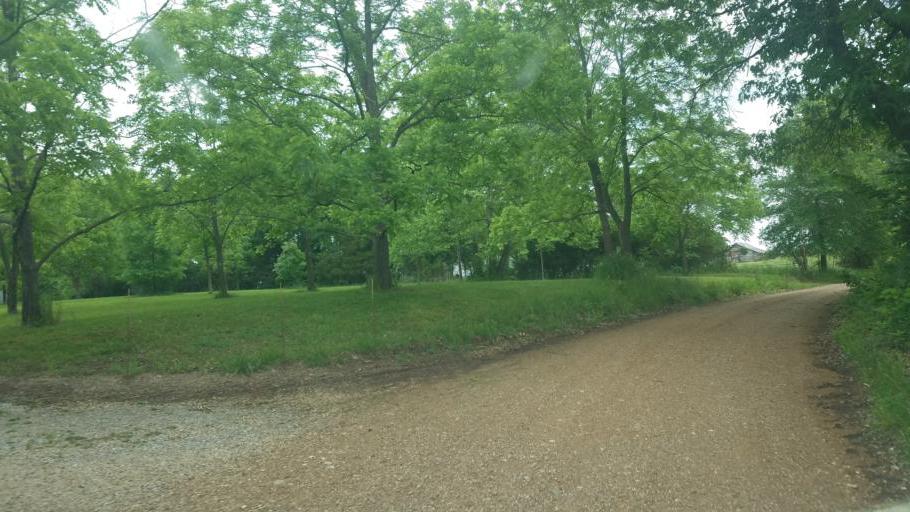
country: US
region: Missouri
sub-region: Moniteau County
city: California
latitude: 38.6187
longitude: -92.6427
